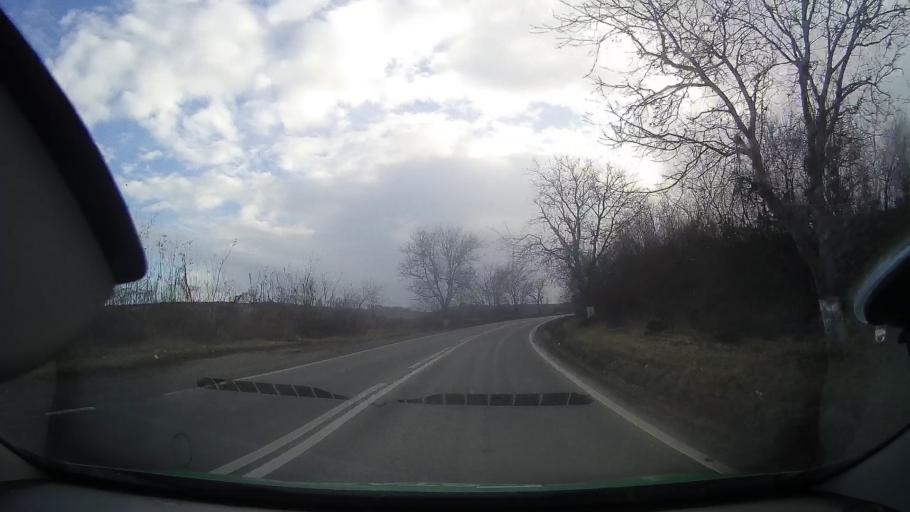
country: RO
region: Mures
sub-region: Comuna Cucerdea
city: Cucerdea
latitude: 46.3617
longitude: 24.2714
